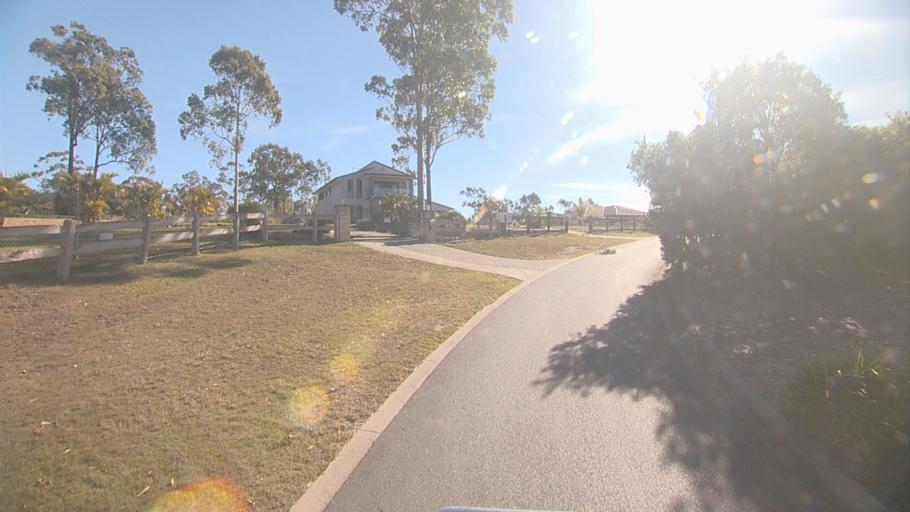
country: AU
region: Queensland
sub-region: Ipswich
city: Springfield Lakes
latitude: -27.7195
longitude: 152.9205
